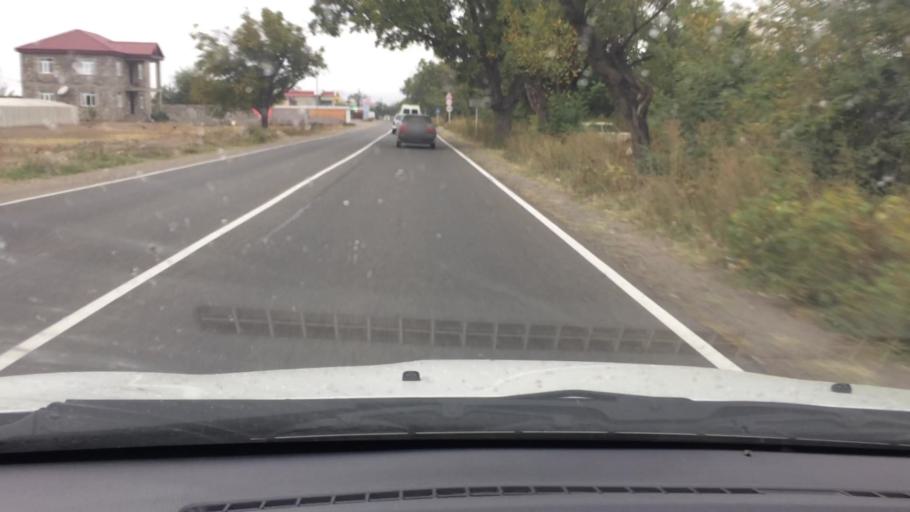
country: GE
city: Naghvarevi
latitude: 41.3969
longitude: 44.8261
